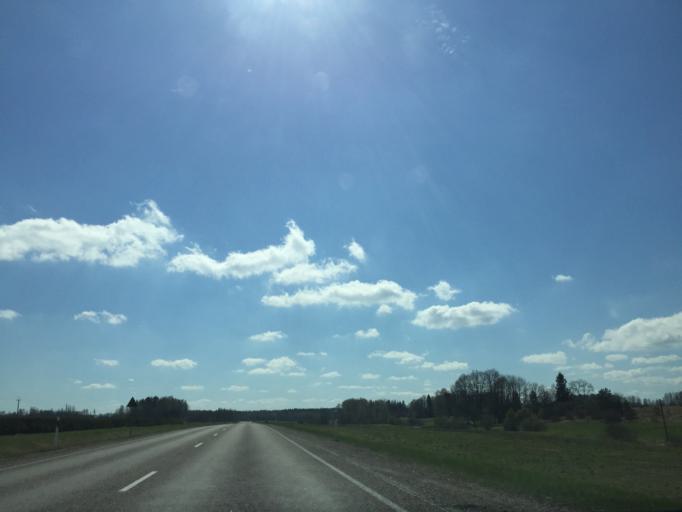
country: EE
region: Valgamaa
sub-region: Torva linn
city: Torva
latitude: 58.0282
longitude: 26.1725
